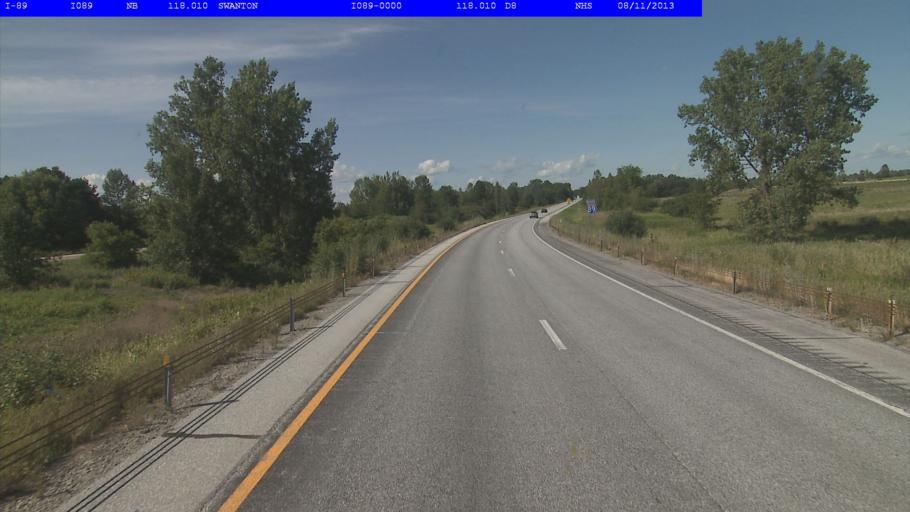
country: US
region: Vermont
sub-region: Franklin County
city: Saint Albans
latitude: 44.8485
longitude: -73.0829
